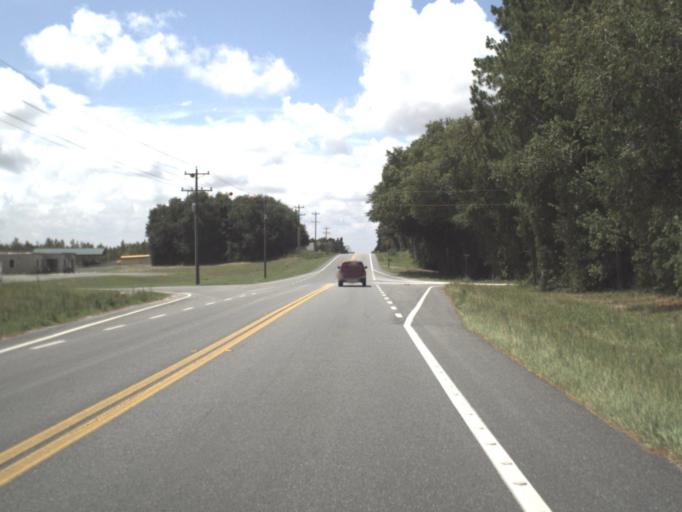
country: US
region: Florida
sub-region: Gilchrist County
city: Trenton
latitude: 29.7860
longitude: -82.8668
